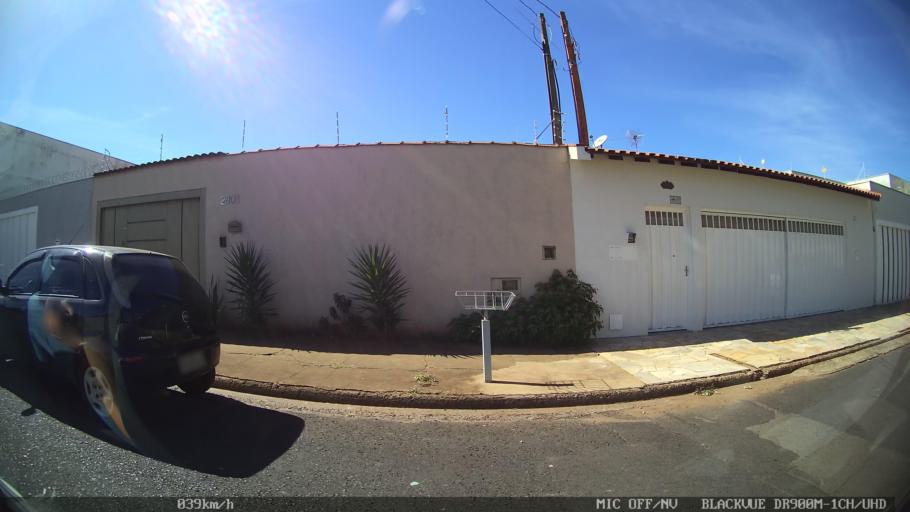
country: BR
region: Sao Paulo
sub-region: Franca
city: Franca
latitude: -20.5430
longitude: -47.3797
